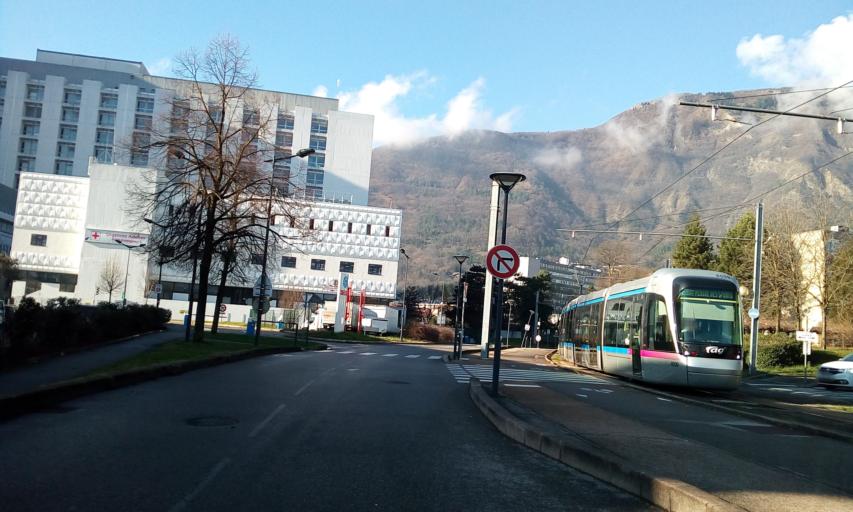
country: FR
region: Rhone-Alpes
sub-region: Departement de l'Isere
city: La Tronche
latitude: 45.1995
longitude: 5.7480
